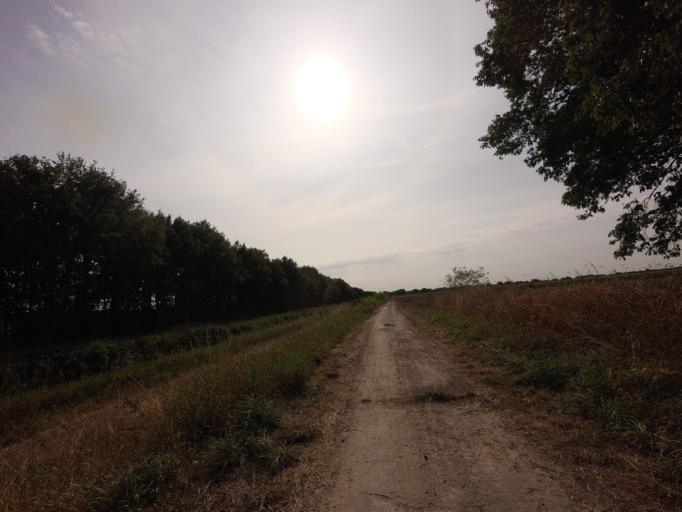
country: NL
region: North Brabant
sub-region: Gemeente Sint Anthonis
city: Sint Anthonis
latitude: 51.5812
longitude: 5.8426
